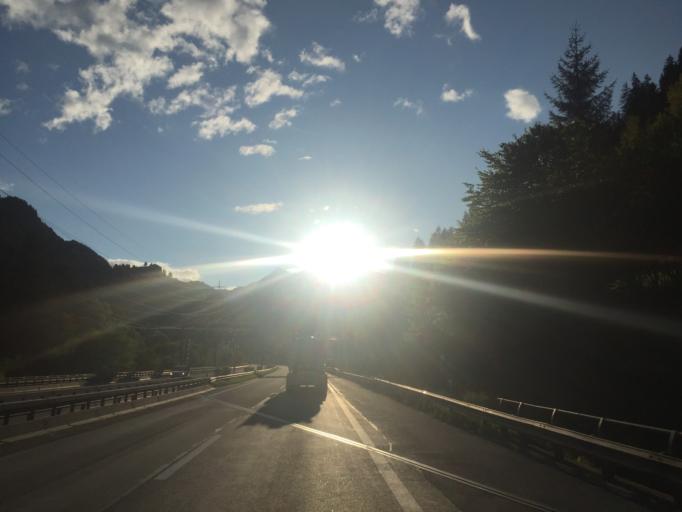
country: CH
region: Ticino
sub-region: Leventina District
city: Airolo
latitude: 46.5183
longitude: 8.6528
